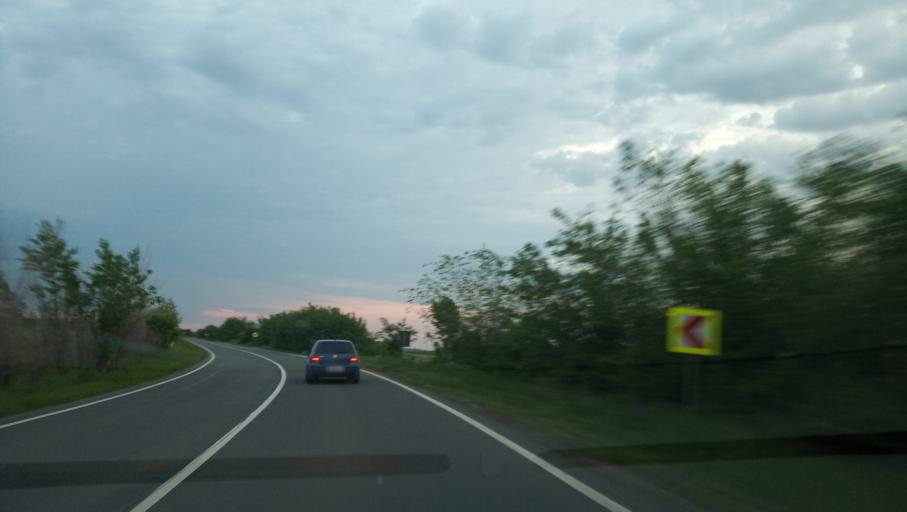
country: RO
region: Timis
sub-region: Comuna Padureni
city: Padureni
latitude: 45.6172
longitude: 21.1954
